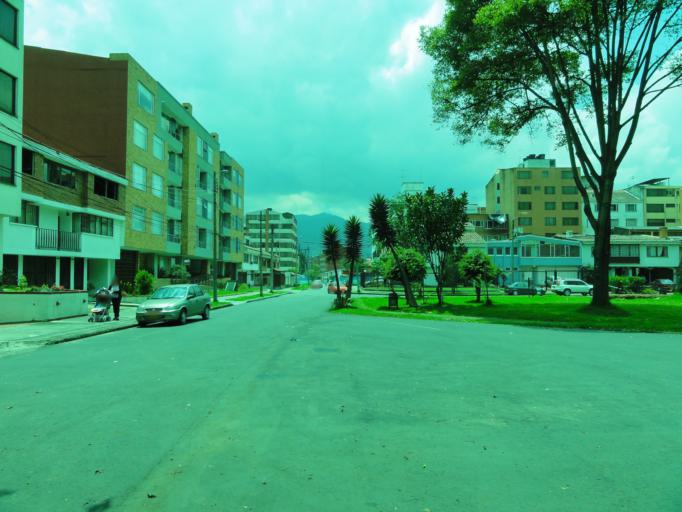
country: CO
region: Bogota D.C.
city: Bogota
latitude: 4.6525
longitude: -74.0837
